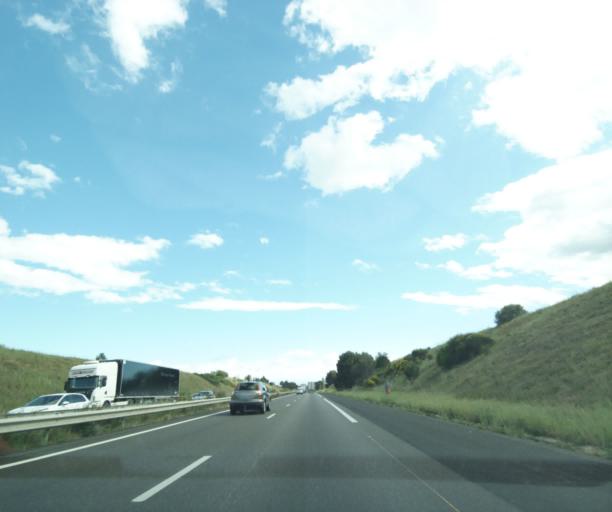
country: FR
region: Languedoc-Roussillon
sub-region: Departement du Gard
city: Garons
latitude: 43.7667
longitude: 4.4214
